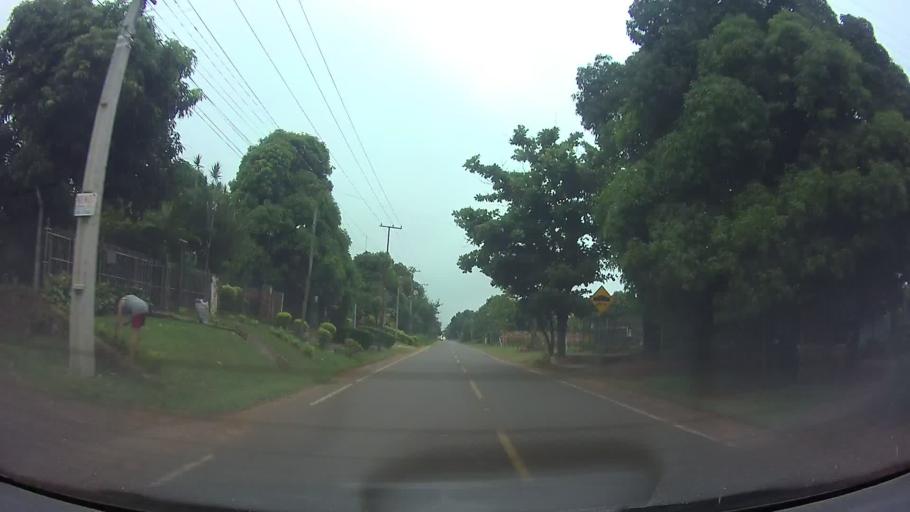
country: PY
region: Central
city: Itaugua
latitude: -25.3775
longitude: -57.3491
